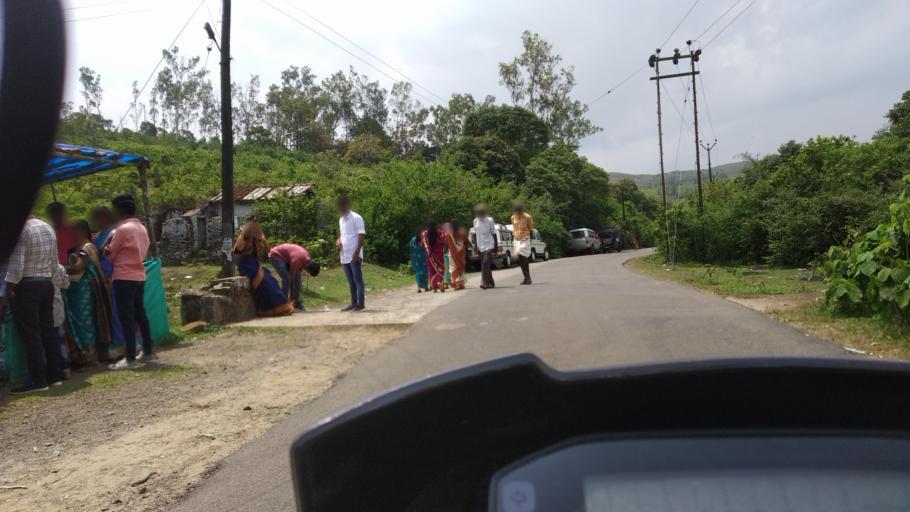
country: IN
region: Kerala
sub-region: Kottayam
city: Erattupetta
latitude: 9.6385
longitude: 76.9316
